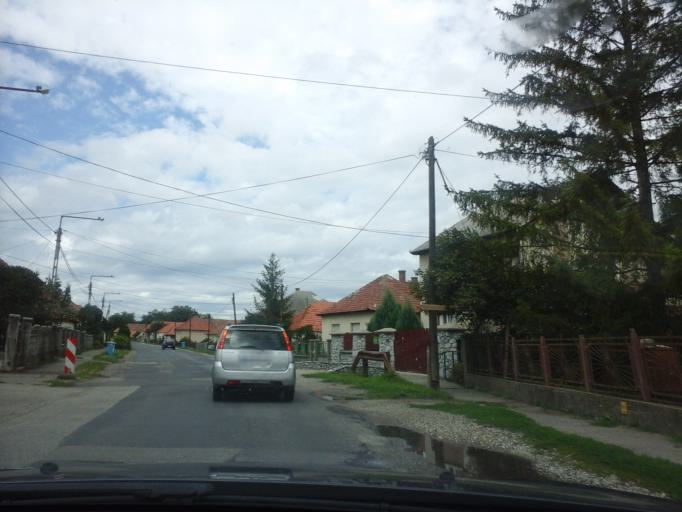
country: HU
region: Borsod-Abauj-Zemplen
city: Izsofalva
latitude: 48.3155
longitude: 20.6212
